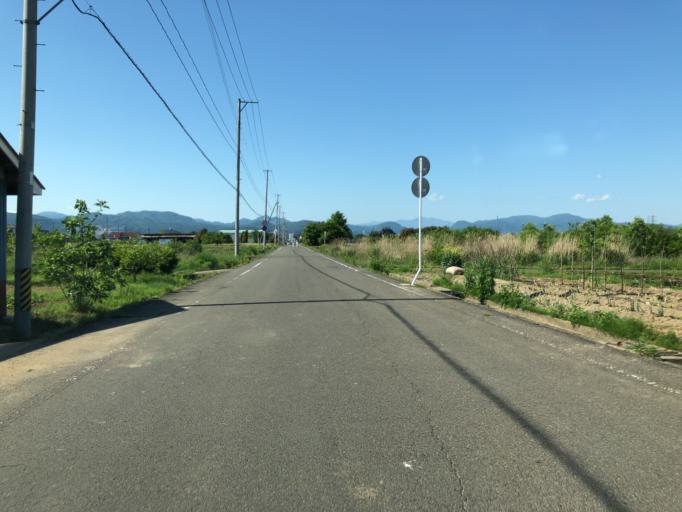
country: JP
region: Fukushima
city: Fukushima-shi
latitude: 37.7326
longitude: 140.4086
